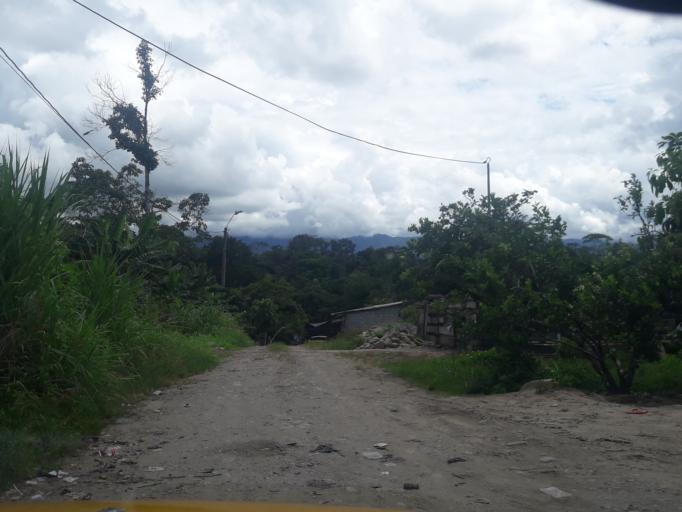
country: EC
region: Napo
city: Tena
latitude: -1.0031
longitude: -77.8206
